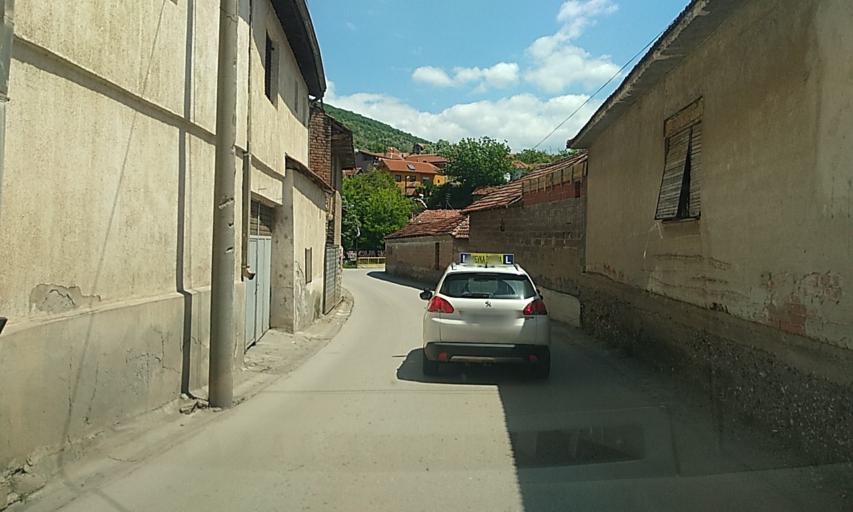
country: RS
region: Central Serbia
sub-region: Nisavski Okrug
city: Nis
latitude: 43.3645
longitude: 21.9660
